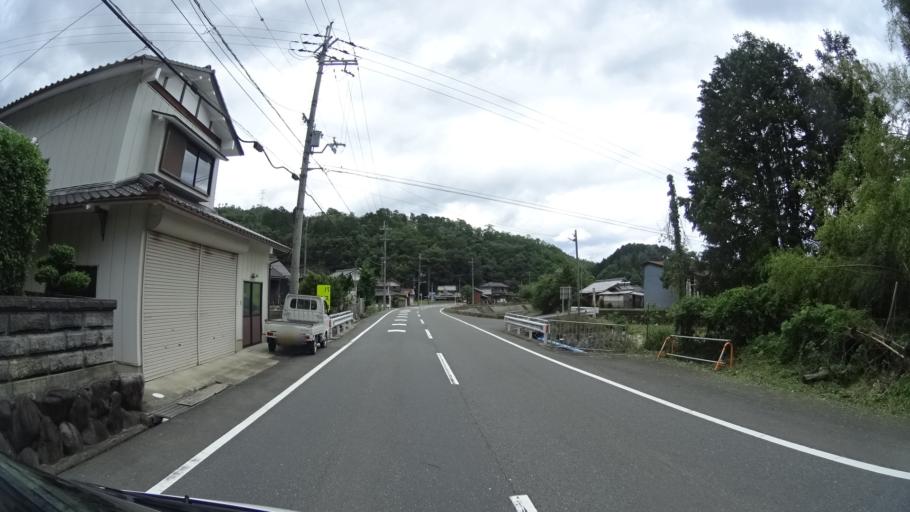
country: JP
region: Kyoto
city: Kameoka
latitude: 35.0910
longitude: 135.4208
